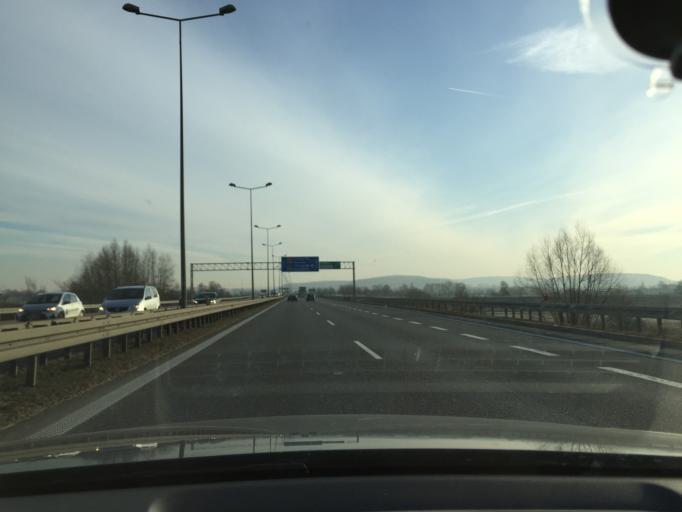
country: PL
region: Lesser Poland Voivodeship
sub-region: Powiat krakowski
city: Kryspinow
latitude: 50.0381
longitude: 19.8114
